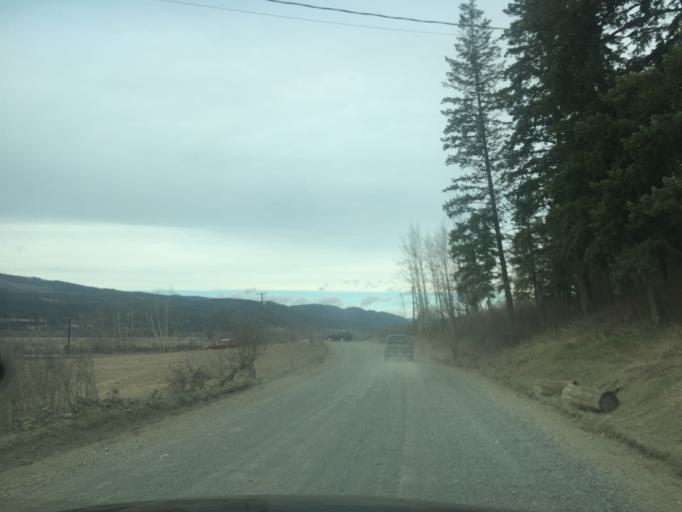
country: CA
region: British Columbia
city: Kamloops
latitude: 51.2466
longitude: -120.1479
